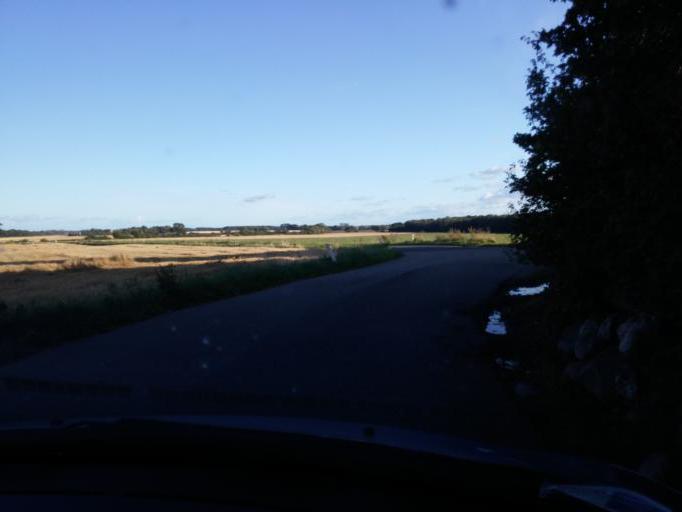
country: DK
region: South Denmark
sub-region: Kerteminde Kommune
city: Munkebo
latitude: 55.4260
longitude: 10.5397
